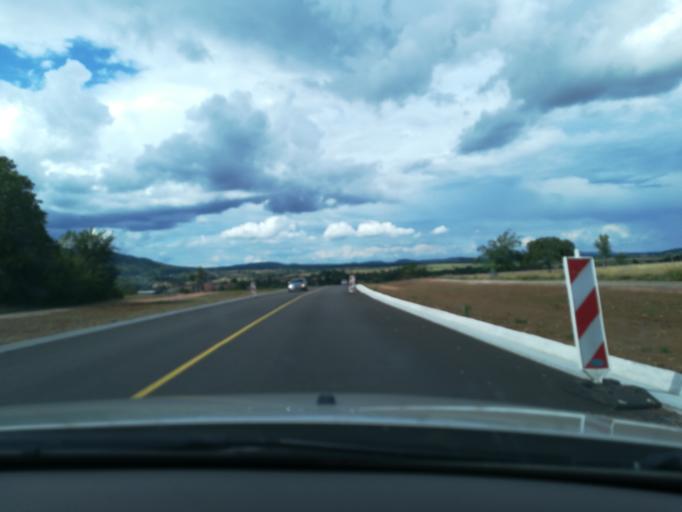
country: FR
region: Alsace
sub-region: Departement du Bas-Rhin
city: Dossenheim-sur-Zinsel
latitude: 48.7940
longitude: 7.4027
